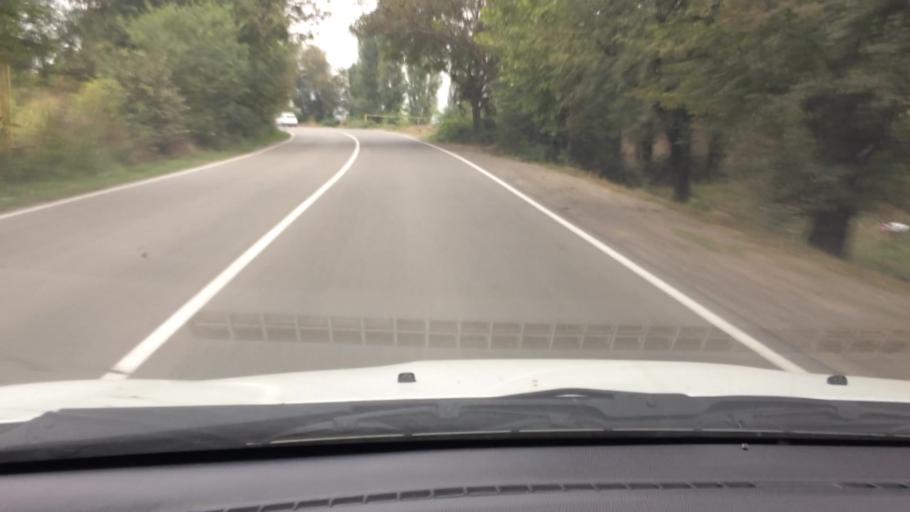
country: AM
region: Tavush
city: Bagratashen
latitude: 41.2605
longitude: 44.7962
